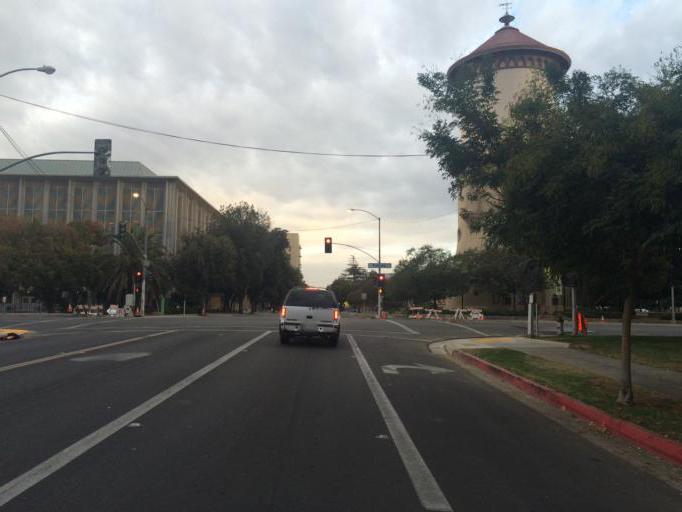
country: US
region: California
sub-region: Fresno County
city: Fresno
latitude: 36.7398
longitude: -119.7876
